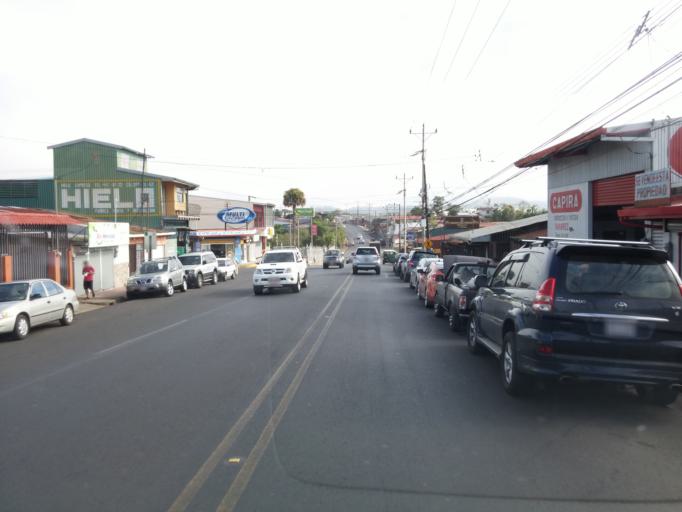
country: CR
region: Alajuela
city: San Ramon
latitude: 10.0937
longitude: -84.4689
